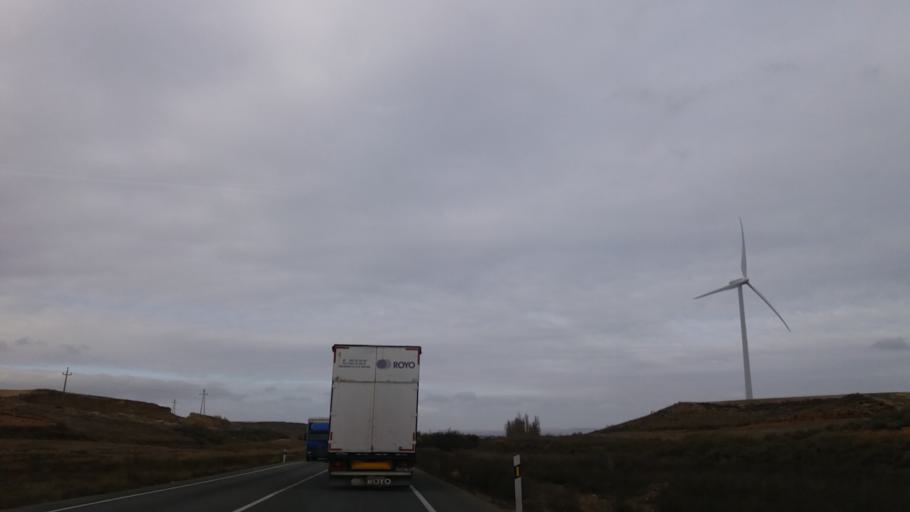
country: ES
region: Aragon
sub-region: Provincia de Zaragoza
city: Mallen
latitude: 41.8853
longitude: -1.4009
